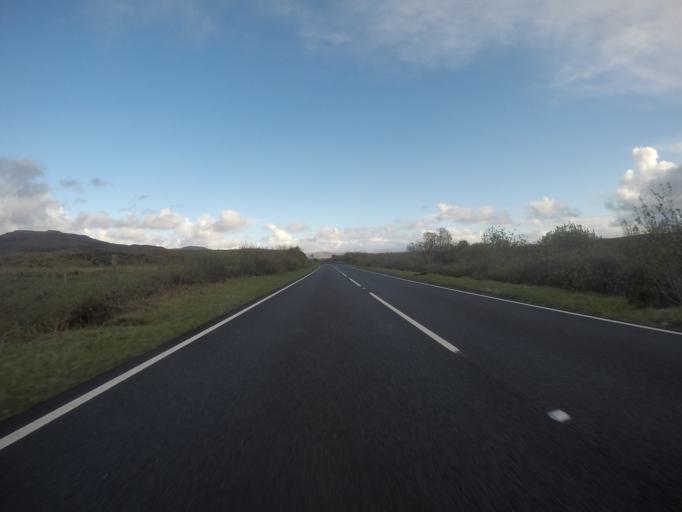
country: GB
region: Scotland
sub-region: Highland
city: Portree
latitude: 57.5021
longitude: -6.3296
